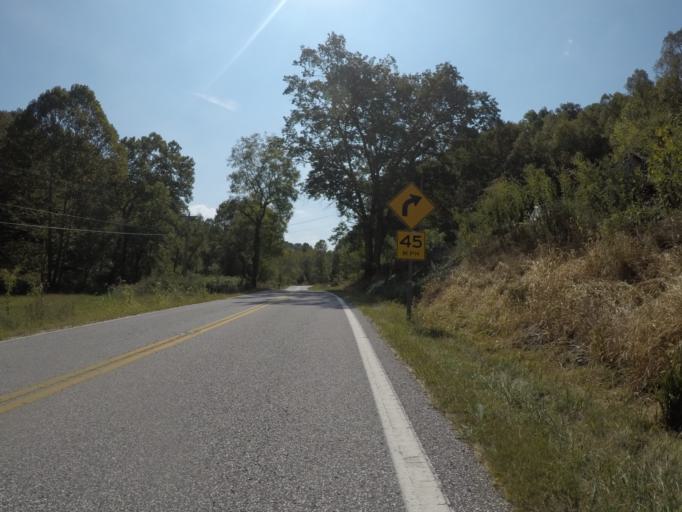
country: US
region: West Virginia
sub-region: Cabell County
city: Lesage
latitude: 38.5620
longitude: -82.3948
